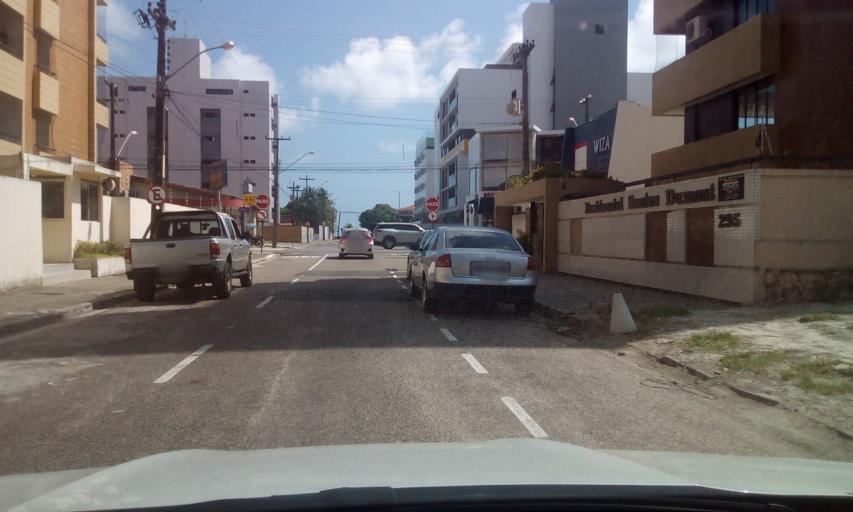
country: BR
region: Paraiba
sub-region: Joao Pessoa
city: Joao Pessoa
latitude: -7.1090
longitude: -34.8279
